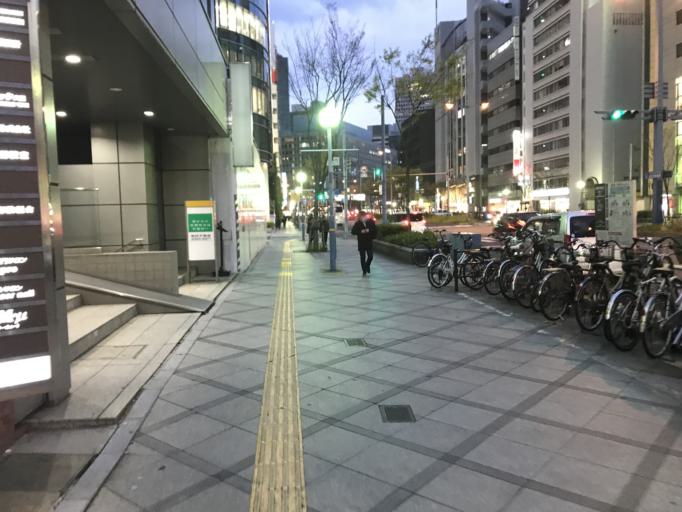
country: JP
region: Osaka
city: Osaka-shi
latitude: 34.6977
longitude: 135.4932
